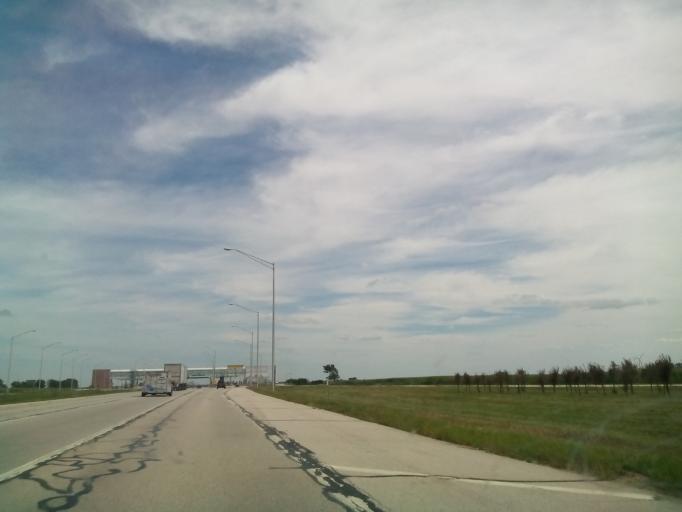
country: US
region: Illinois
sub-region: DeKalb County
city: Malta
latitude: 41.8996
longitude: -88.8795
